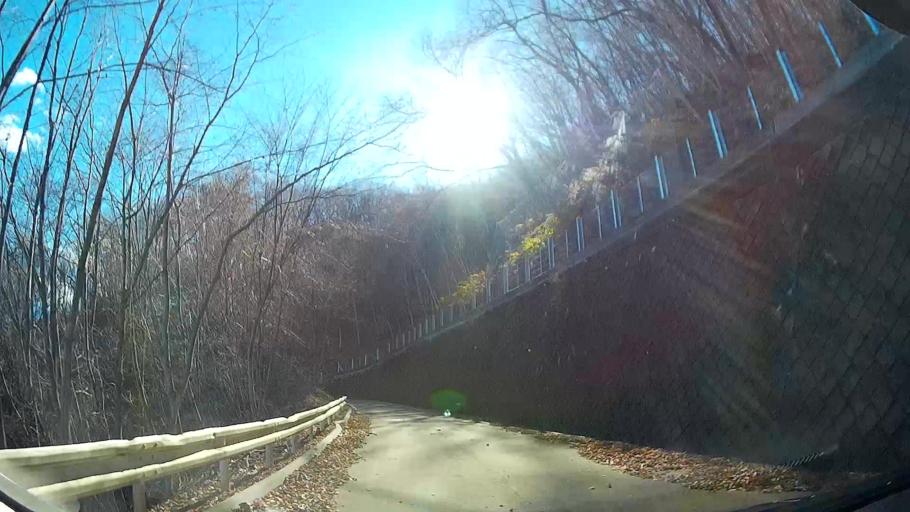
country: JP
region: Yamanashi
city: Otsuki
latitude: 35.7308
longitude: 138.9466
